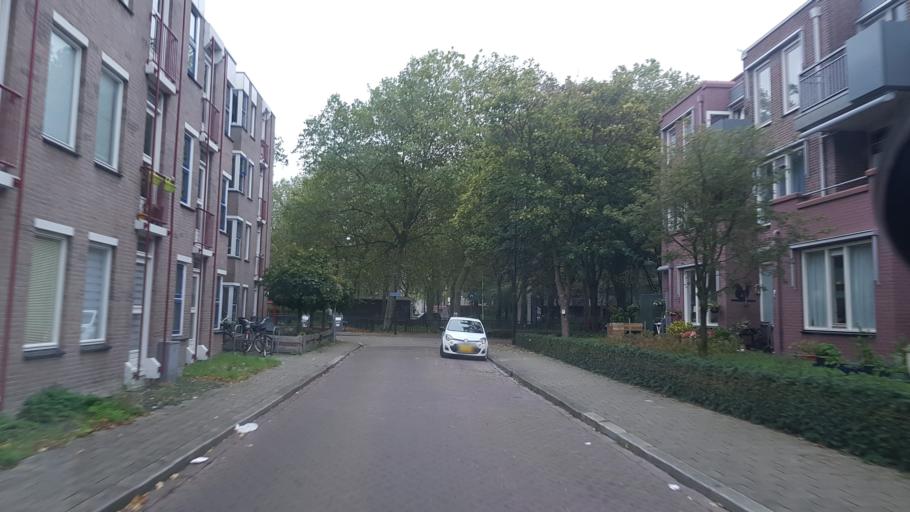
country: NL
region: Gelderland
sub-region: Gemeente Apeldoorn
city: Apeldoorn
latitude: 52.2152
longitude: 5.9528
